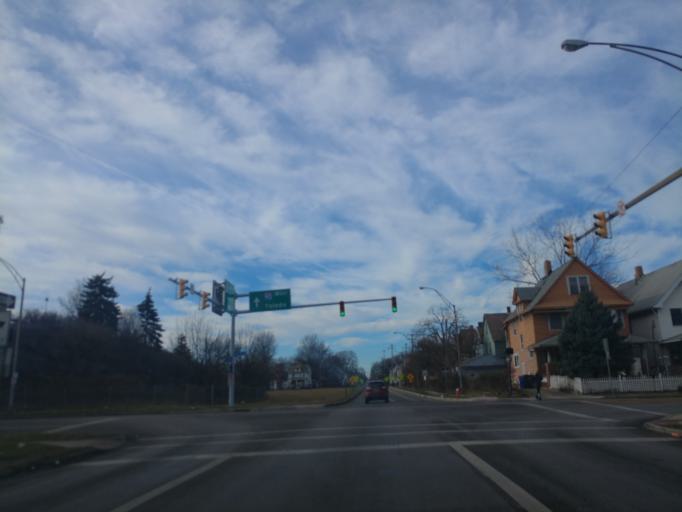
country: US
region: Ohio
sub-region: Cuyahoga County
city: Brooklyn
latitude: 41.4705
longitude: -81.7508
